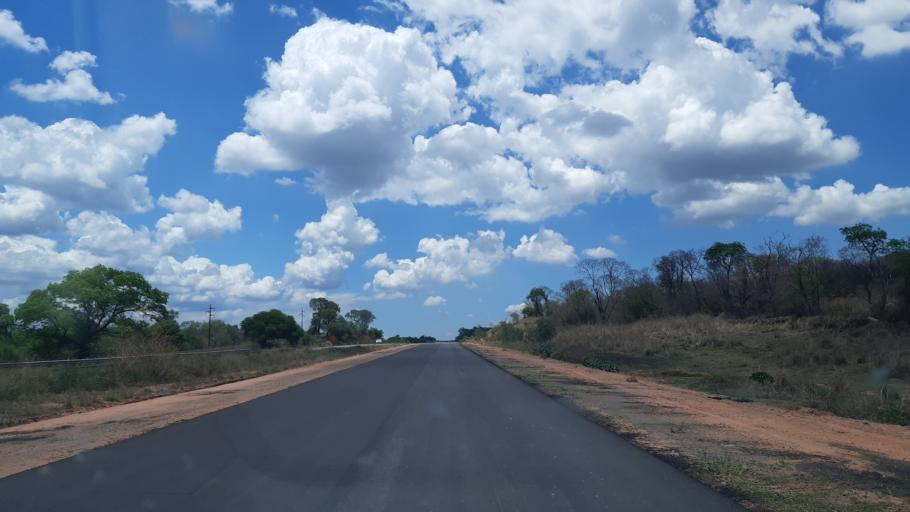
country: AR
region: Jujuy
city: La Mendieta
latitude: -24.4128
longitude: -64.9973
